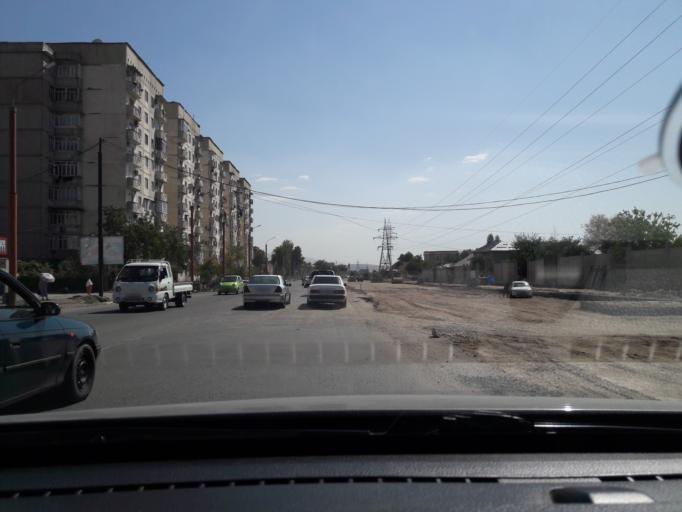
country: TJ
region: Dushanbe
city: Dushanbe
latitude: 38.5350
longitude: 68.7396
